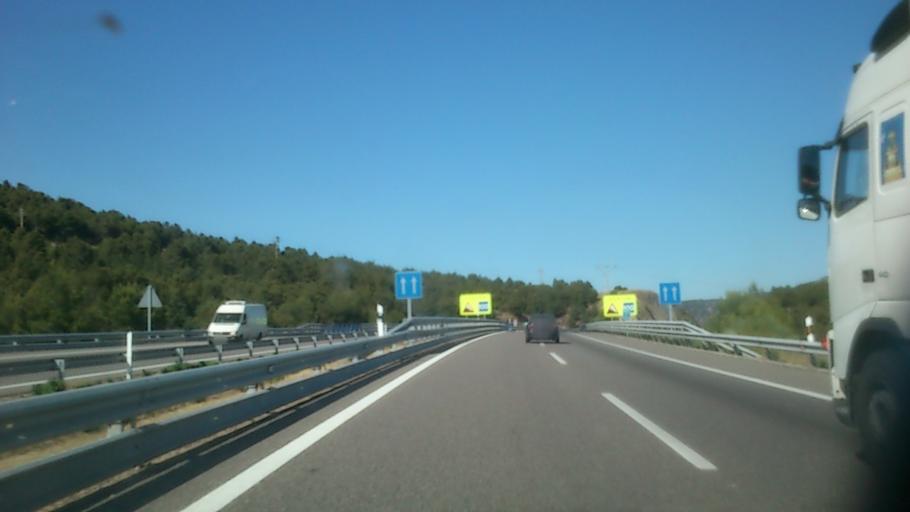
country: ES
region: Aragon
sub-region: Provincia de Zaragoza
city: Paracuellos de la Ribera
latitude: 41.3901
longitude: -1.5630
